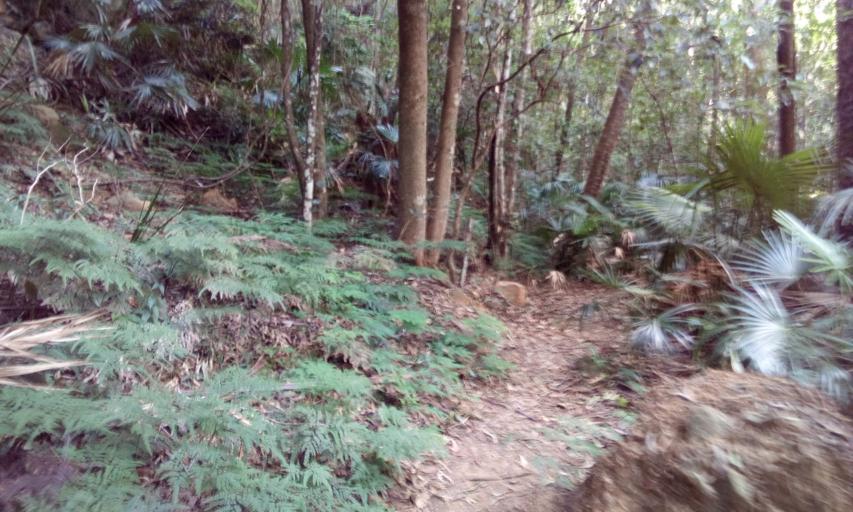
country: AU
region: New South Wales
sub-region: Wollongong
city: Cordeaux Heights
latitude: -34.4422
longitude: 150.7952
